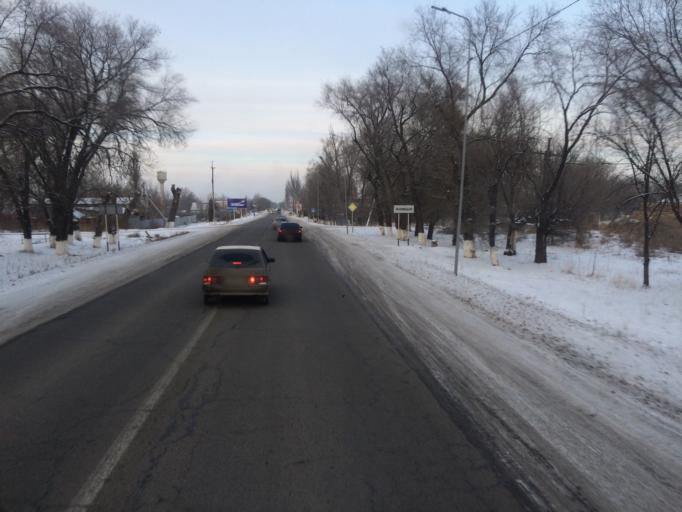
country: KZ
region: Almaty Oblysy
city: Burunday
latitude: 43.2658
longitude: 76.6701
